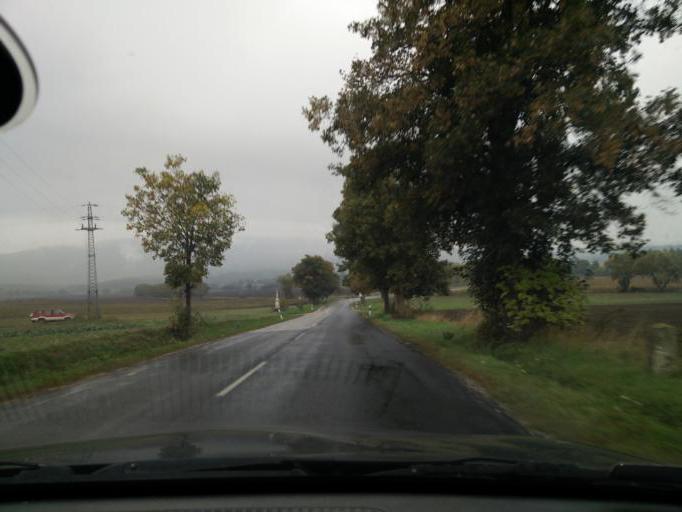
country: HU
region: Komarom-Esztergom
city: Tarjan
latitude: 47.6371
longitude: 18.5143
